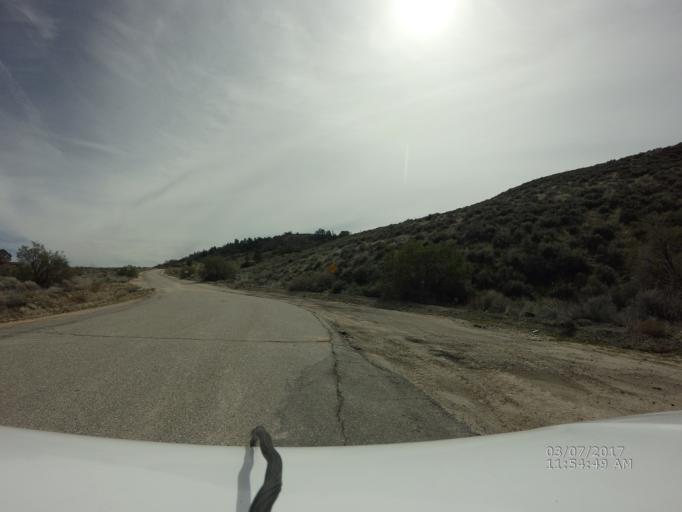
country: US
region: California
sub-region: Kern County
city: Lebec
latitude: 34.7647
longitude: -118.7329
